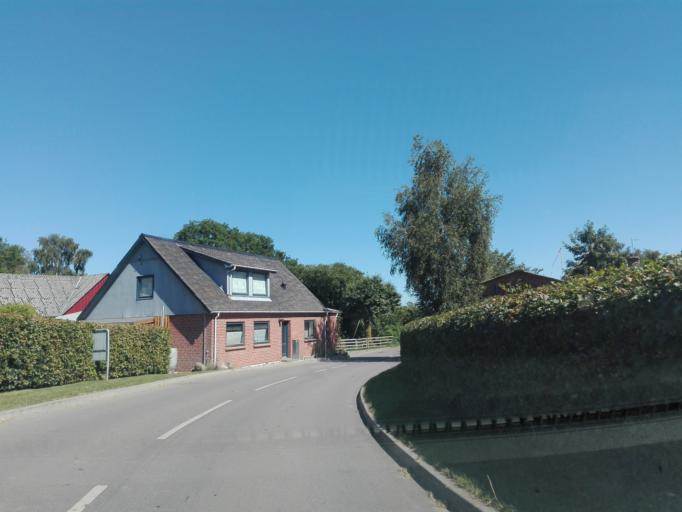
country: DK
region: Central Jutland
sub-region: Arhus Kommune
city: Malling
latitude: 55.9918
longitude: 10.2221
